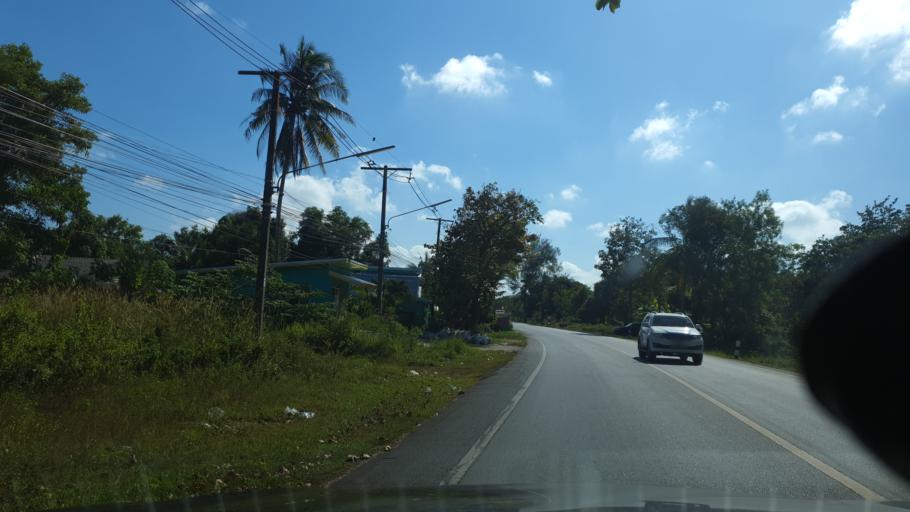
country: TH
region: Krabi
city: Krabi
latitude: 8.0281
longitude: 98.8712
